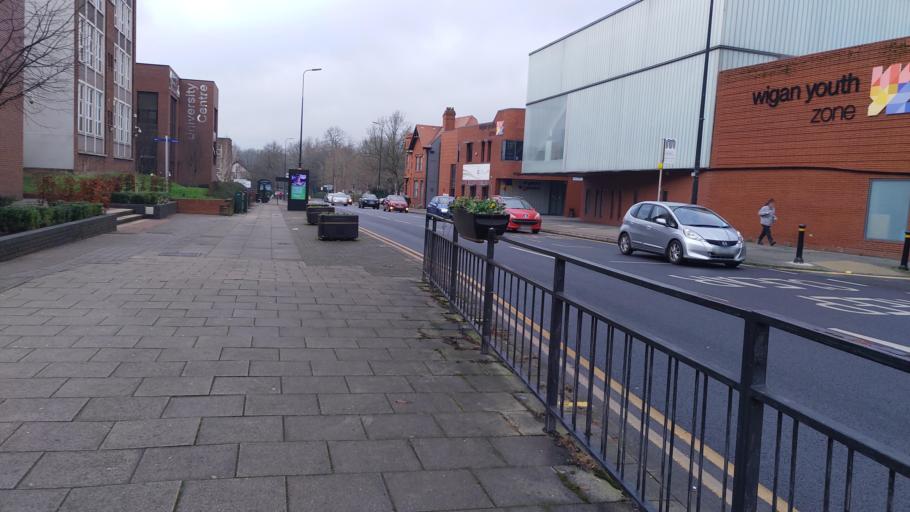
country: GB
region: England
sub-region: Borough of Wigan
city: Ince-in-Makerfield
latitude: 53.5488
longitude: -2.6344
